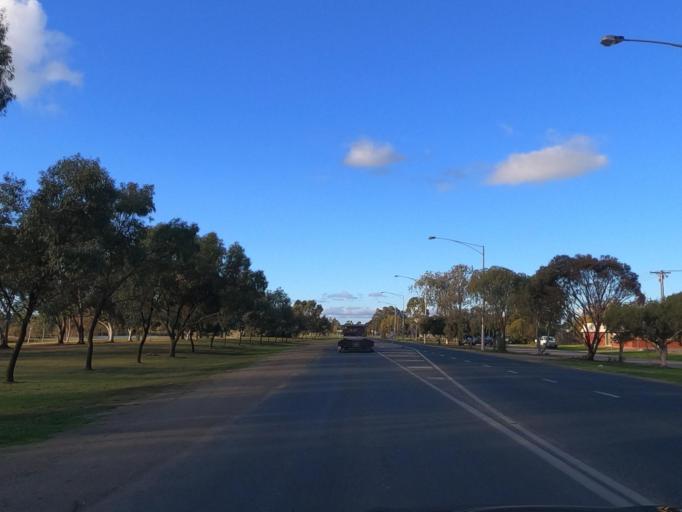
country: AU
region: Victoria
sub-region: Swan Hill
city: Swan Hill
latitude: -35.3414
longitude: 143.5358
